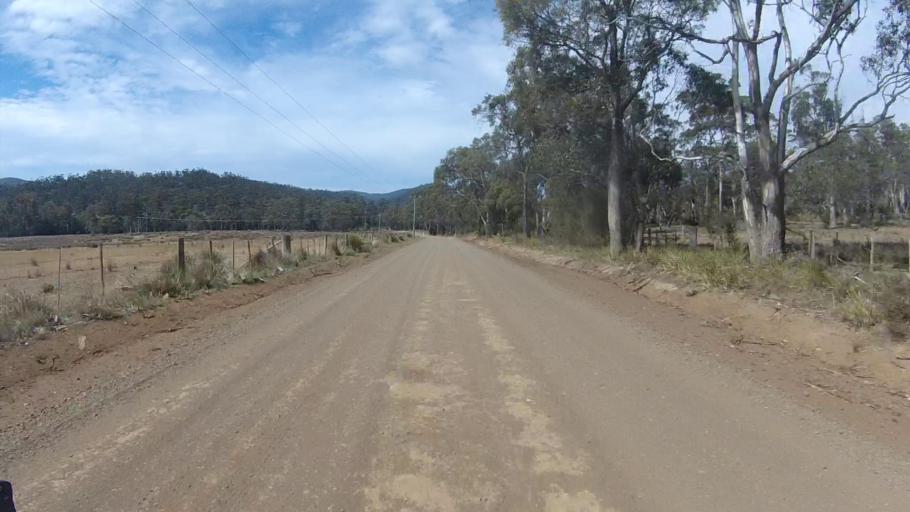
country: AU
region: Tasmania
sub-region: Sorell
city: Sorell
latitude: -42.6447
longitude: 147.9002
